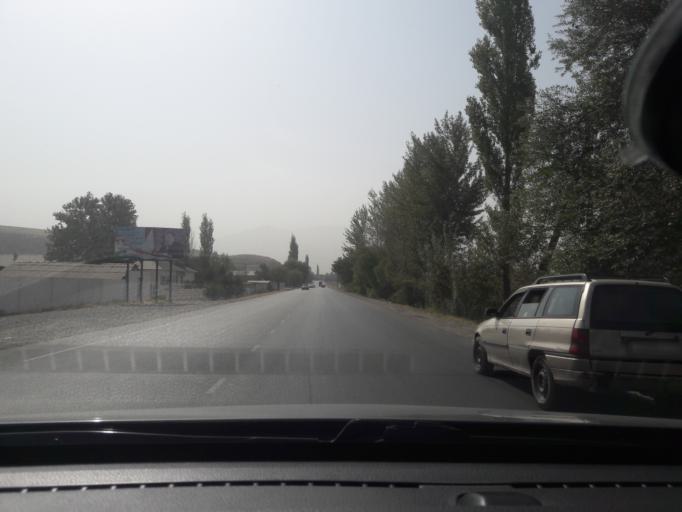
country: TJ
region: Republican Subordination
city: Vahdat
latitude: 38.5258
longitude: 69.0273
